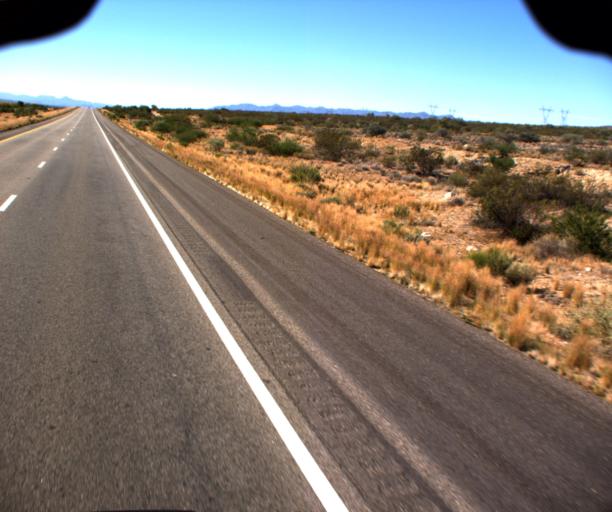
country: US
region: Arizona
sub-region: Mohave County
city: Kingman
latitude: 34.8849
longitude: -113.6498
